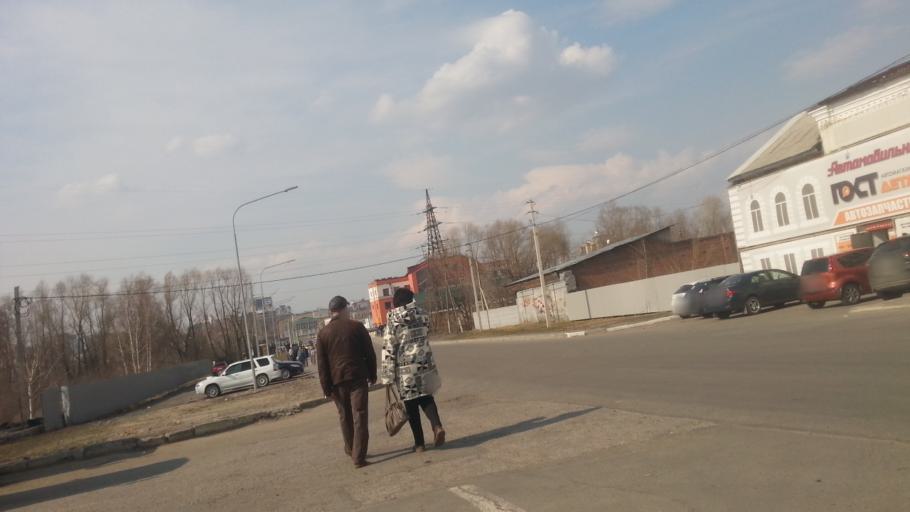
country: RU
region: Altai Krai
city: Zaton
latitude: 53.3267
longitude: 83.7928
